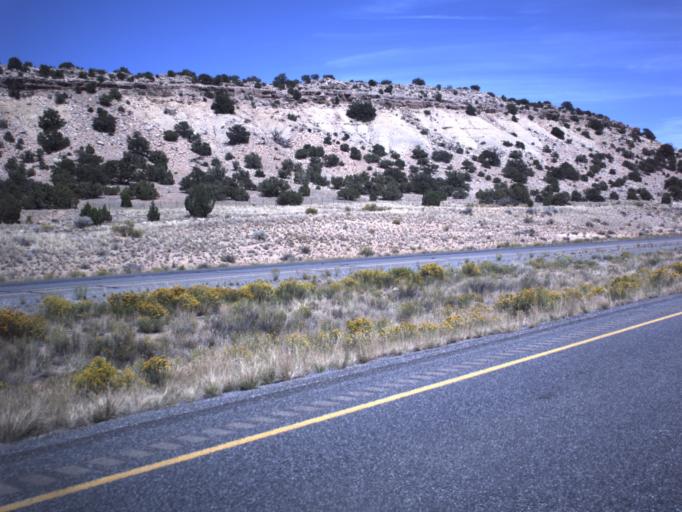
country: US
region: Utah
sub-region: Emery County
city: Castle Dale
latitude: 38.9049
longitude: -110.5445
